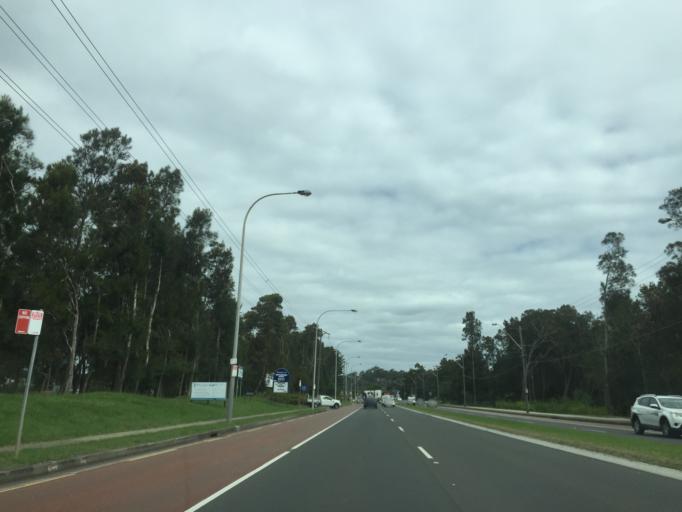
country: AU
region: New South Wales
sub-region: Pittwater
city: Warriewood
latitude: -33.6950
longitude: 151.3027
